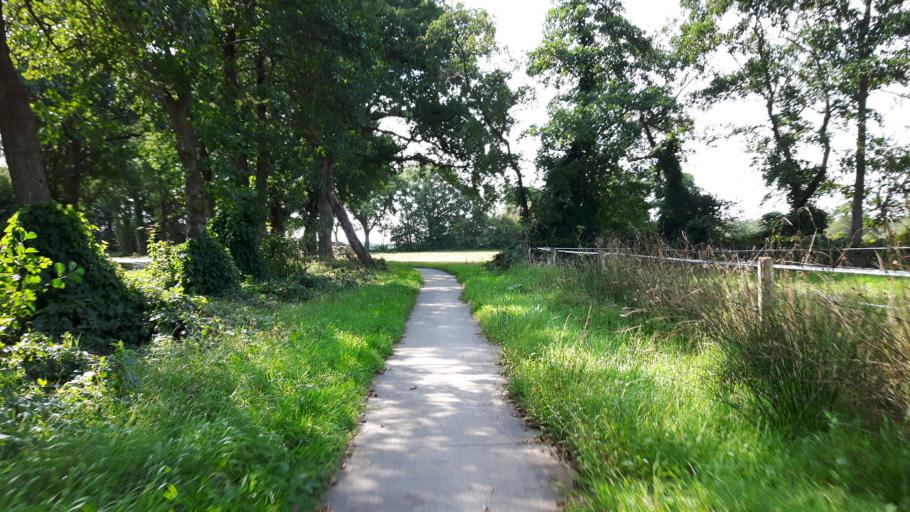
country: NL
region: Groningen
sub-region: Gemeente Leek
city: Leek
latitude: 53.1223
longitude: 6.4462
